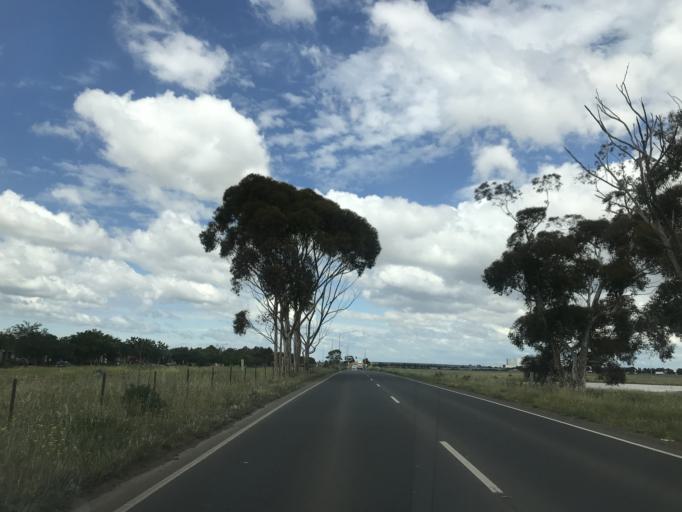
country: AU
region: Victoria
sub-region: Brimbank
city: Derrimut
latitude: -37.7845
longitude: 144.7544
